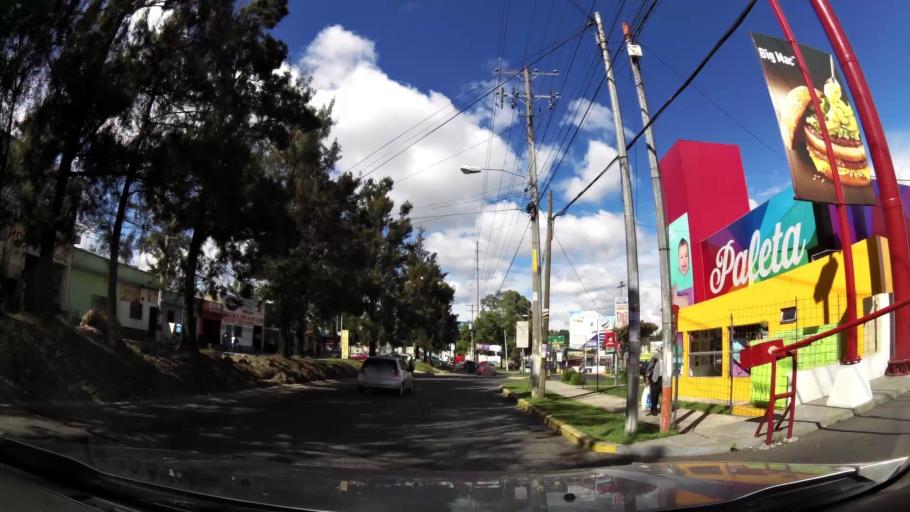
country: GT
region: Guatemala
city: Mixco
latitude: 14.6561
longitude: -90.5692
